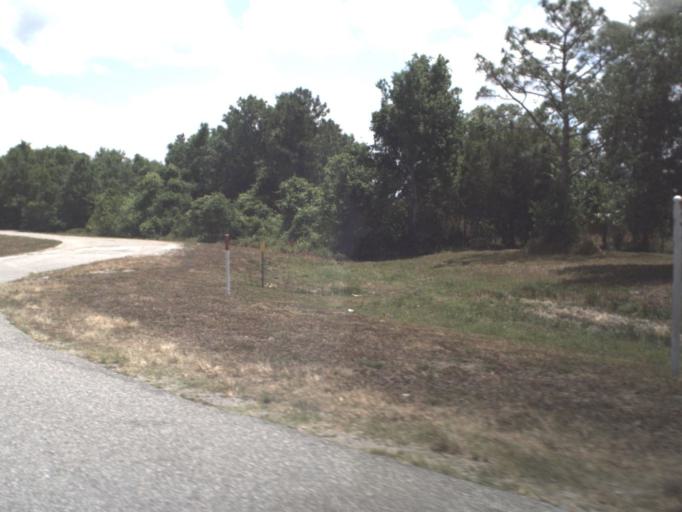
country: US
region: Florida
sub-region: Orange County
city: Wedgefield
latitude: 28.4523
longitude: -81.0304
